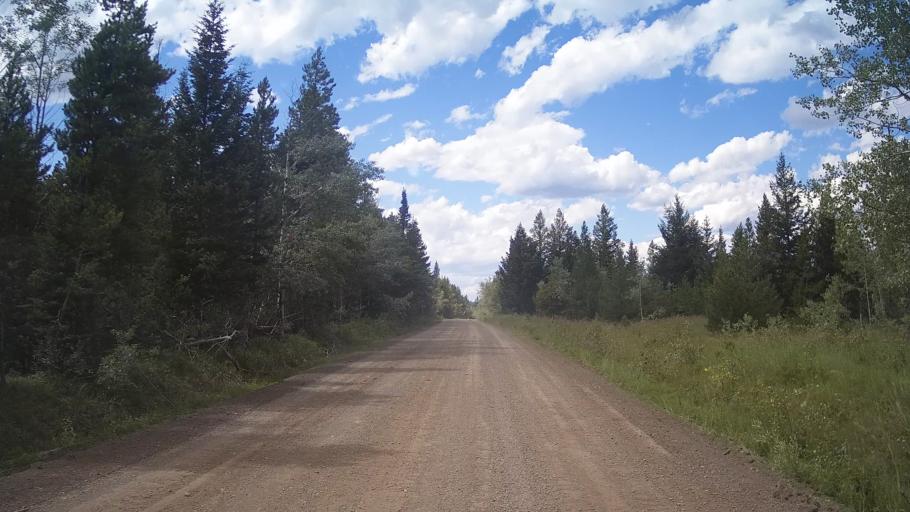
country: CA
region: British Columbia
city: Lillooet
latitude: 51.3265
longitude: -121.8818
